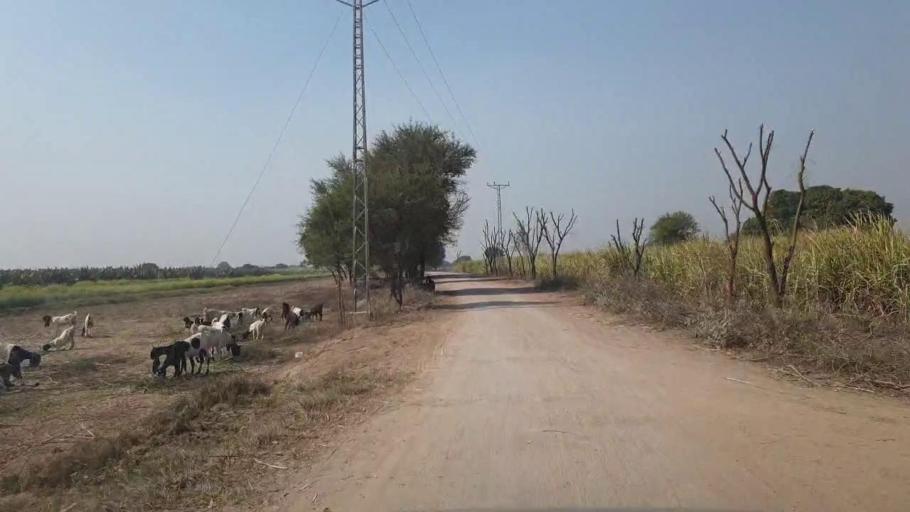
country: PK
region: Sindh
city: Tando Jam
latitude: 25.3292
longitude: 68.6180
